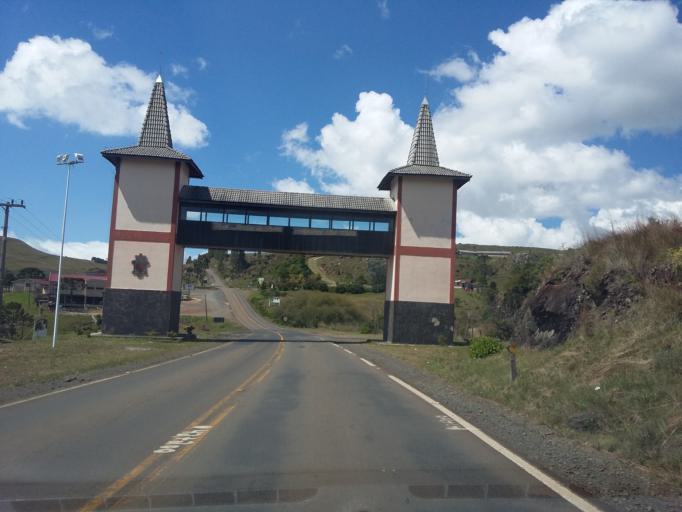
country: BR
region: Santa Catarina
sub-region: Lauro Muller
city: Lauro Muller
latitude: -28.3467
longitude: -49.6013
